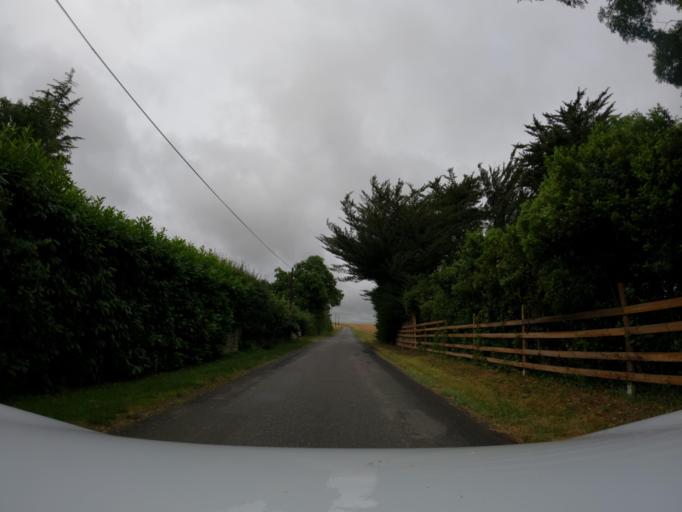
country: FR
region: Pays de la Loire
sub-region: Departement de la Vendee
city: Maillezais
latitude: 46.4044
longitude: -0.7135
